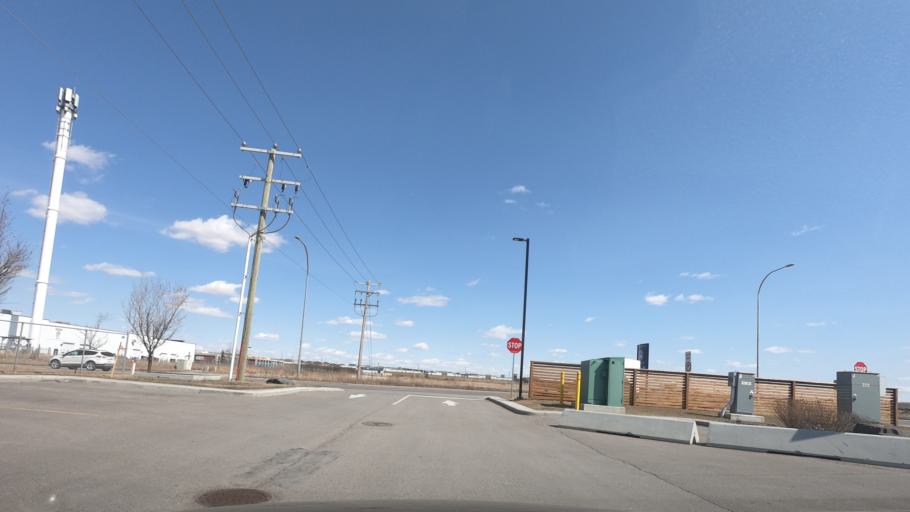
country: CA
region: Alberta
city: Airdrie
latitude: 51.2575
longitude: -114.0055
